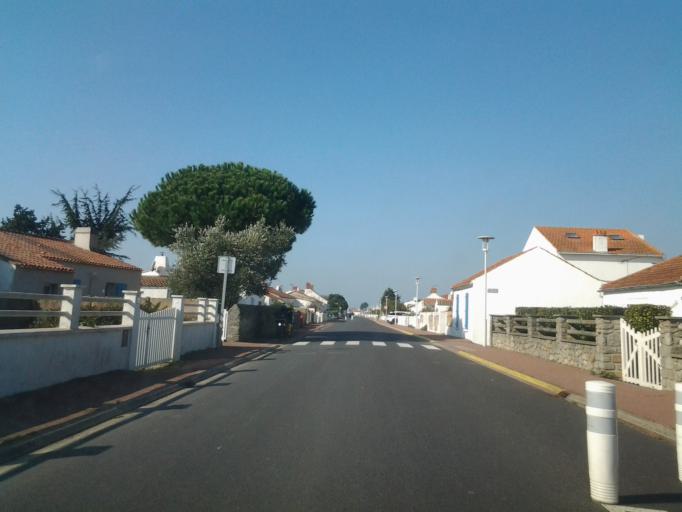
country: FR
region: Pays de la Loire
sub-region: Departement de la Vendee
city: La Gueriniere
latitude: 46.9674
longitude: -2.2214
